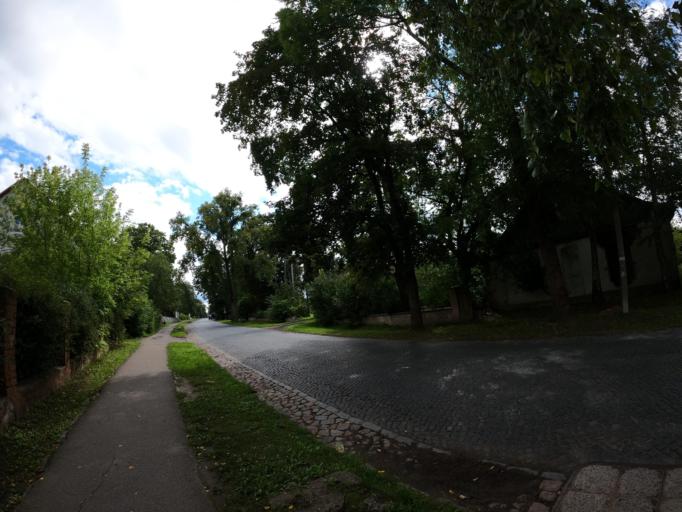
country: RU
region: Kaliningrad
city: Zheleznodorozhnyy
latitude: 54.3553
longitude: 21.3082
